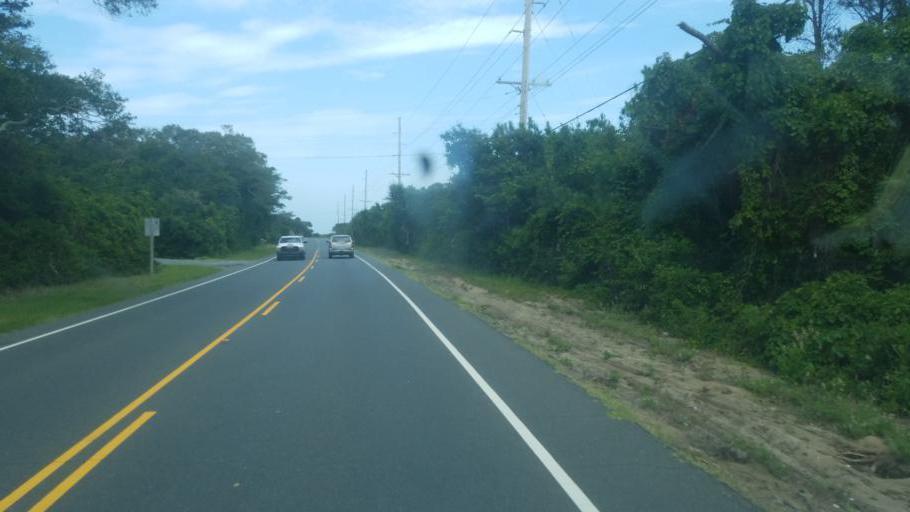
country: US
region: North Carolina
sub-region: Dare County
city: Buxton
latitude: 35.2626
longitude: -75.5682
